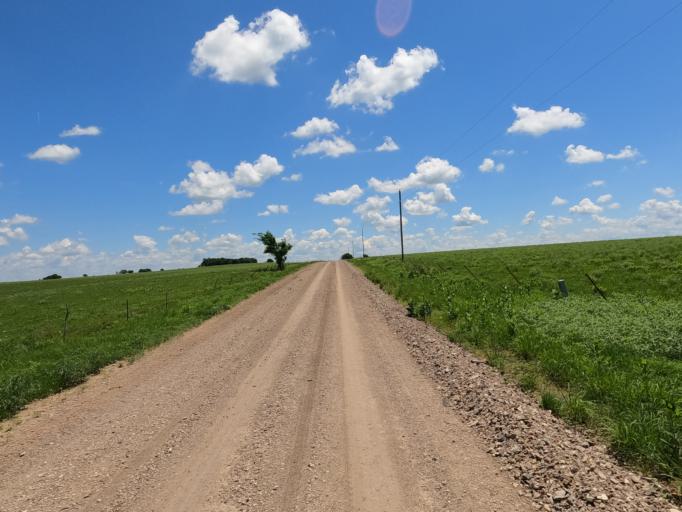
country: US
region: Kansas
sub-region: Chase County
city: Cottonwood Falls
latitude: 38.2167
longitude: -96.7655
